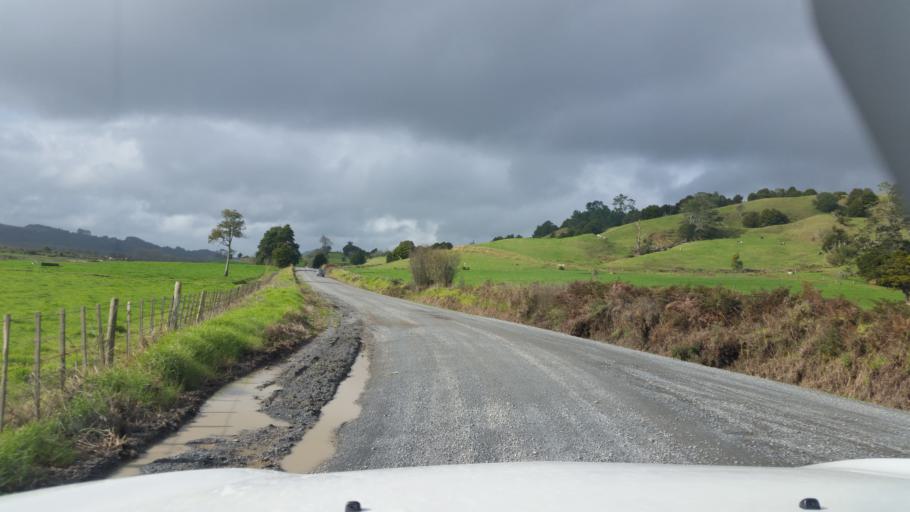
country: NZ
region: Northland
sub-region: Whangarei
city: Maungatapere
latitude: -35.6119
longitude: 174.1693
